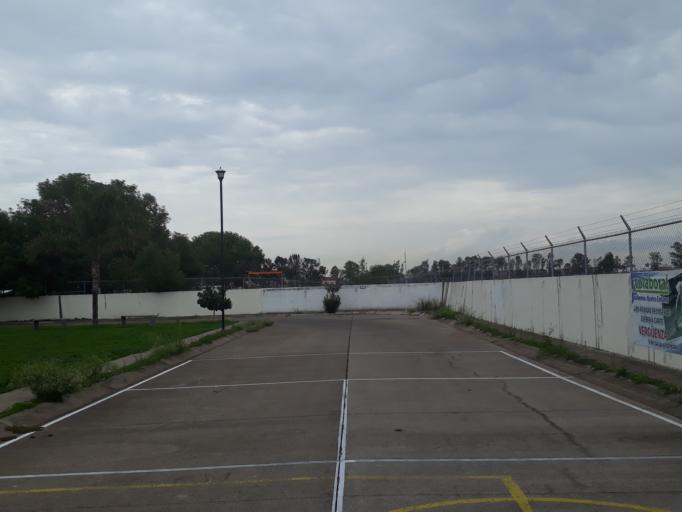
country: MX
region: Aguascalientes
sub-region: Aguascalientes
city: La Loma de los Negritos
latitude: 21.8416
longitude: -102.3300
